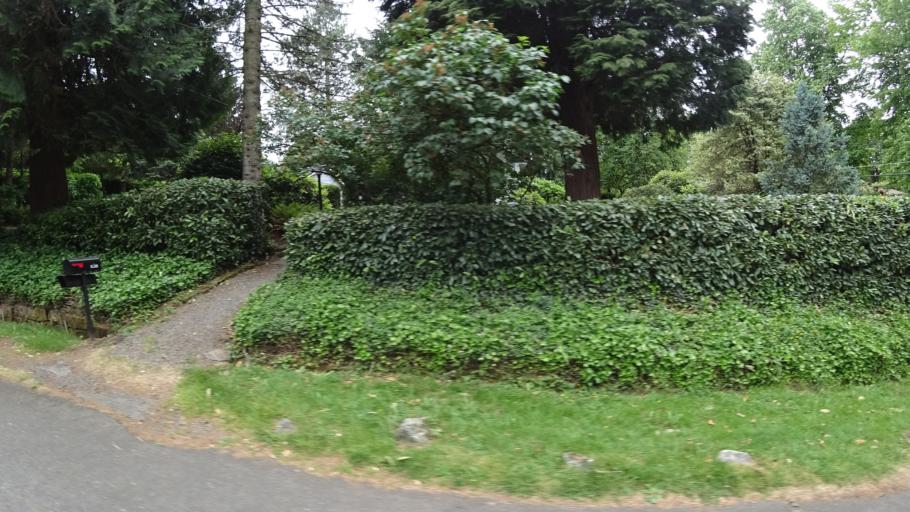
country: US
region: Oregon
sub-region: Clackamas County
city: Lake Oswego
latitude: 45.4589
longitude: -122.6779
